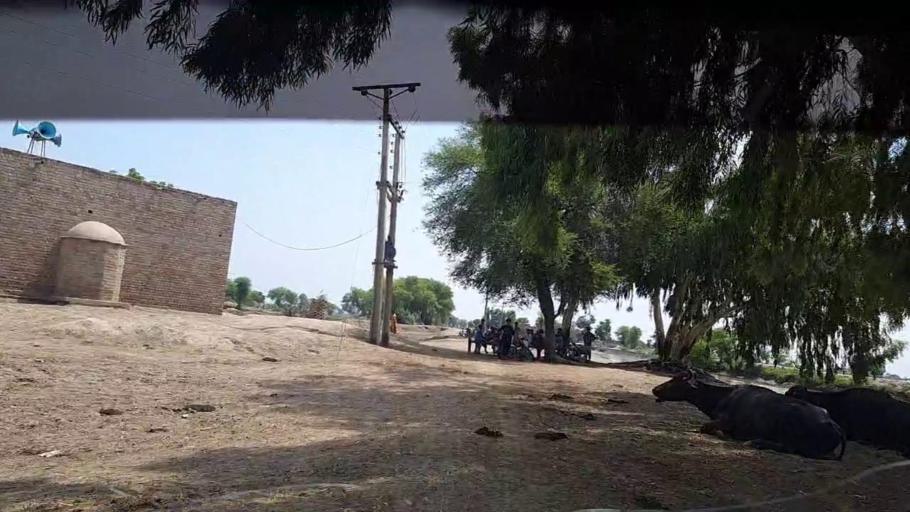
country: PK
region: Sindh
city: Tangwani
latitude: 28.2278
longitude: 68.9009
